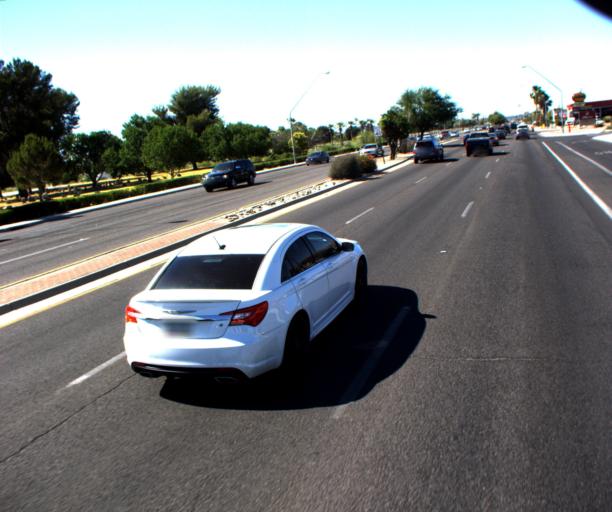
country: US
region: Arizona
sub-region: Pima County
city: Flowing Wells
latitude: 32.2651
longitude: -110.9780
